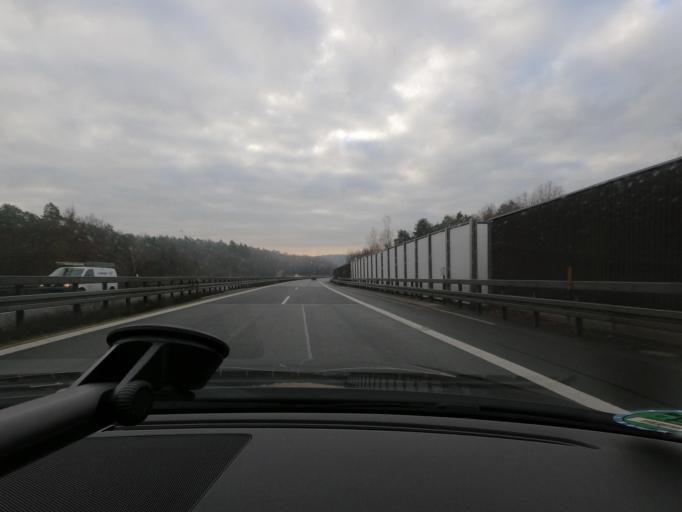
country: DE
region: Bavaria
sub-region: Upper Franconia
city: Zapfendorf
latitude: 50.0228
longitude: 10.9500
